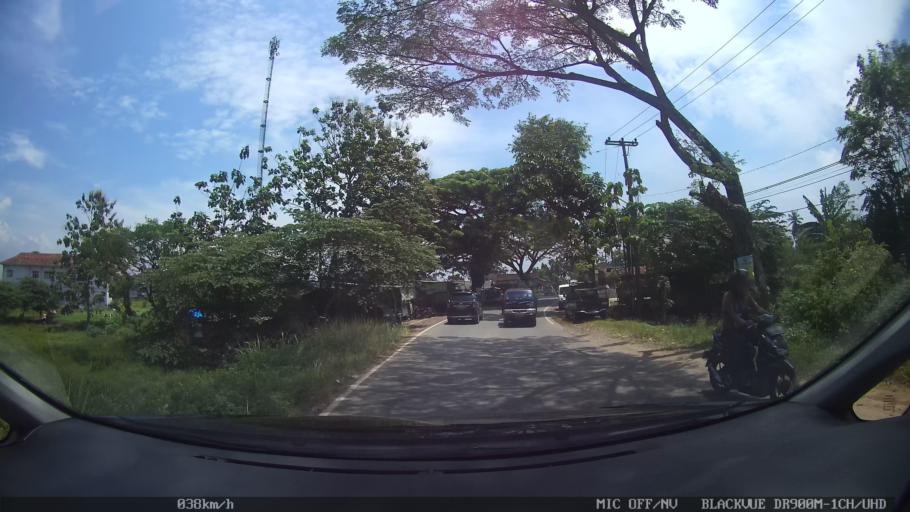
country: ID
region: Lampung
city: Kedaton
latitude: -5.3582
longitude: 105.2886
